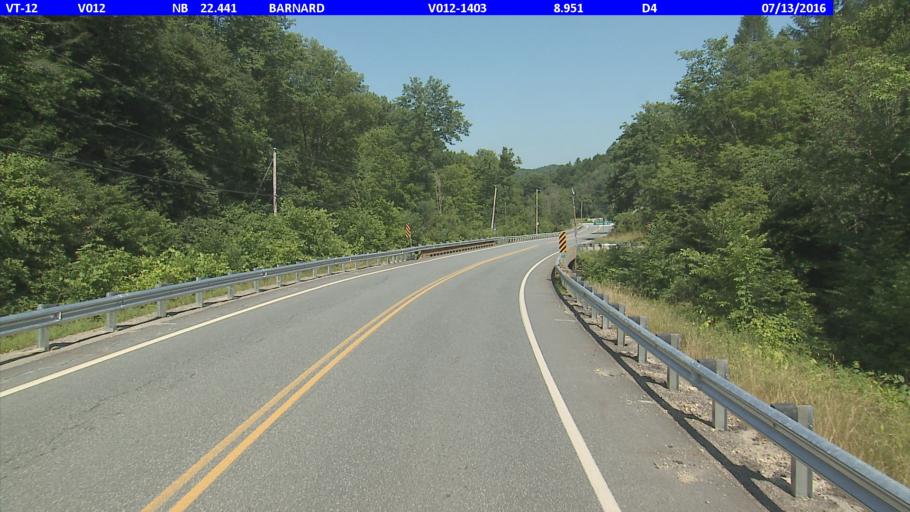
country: US
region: Vermont
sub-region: Orange County
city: Randolph
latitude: 43.7838
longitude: -72.6397
